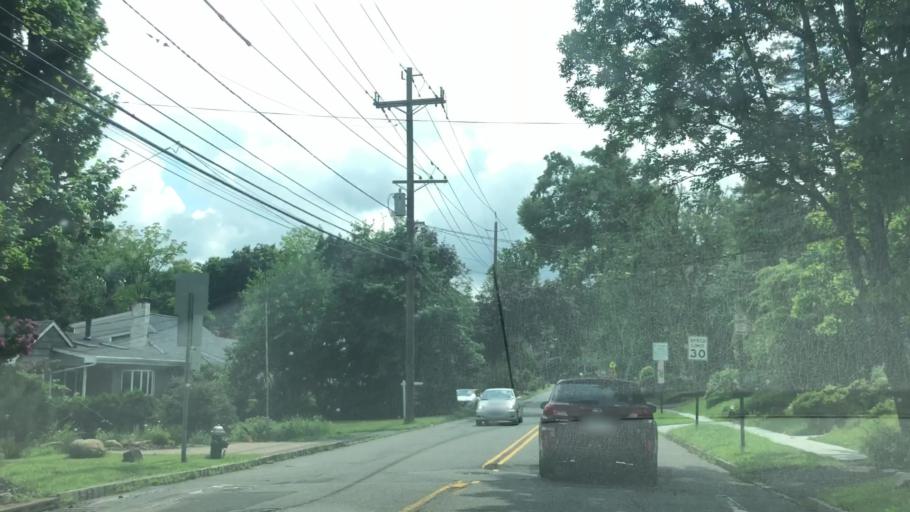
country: US
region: New Jersey
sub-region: Passaic County
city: Little Falls
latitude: 40.8600
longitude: -74.2031
